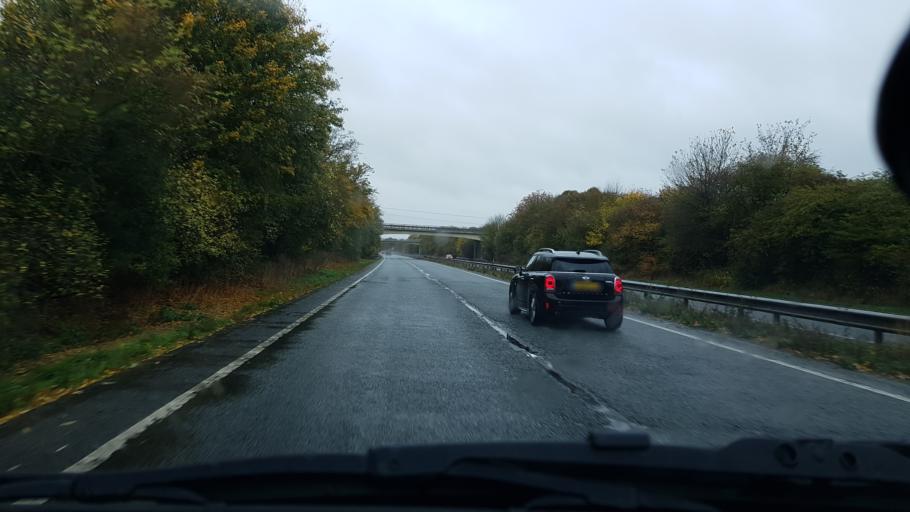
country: GB
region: England
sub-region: Oxfordshire
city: Witney
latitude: 51.7772
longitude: -1.5114
